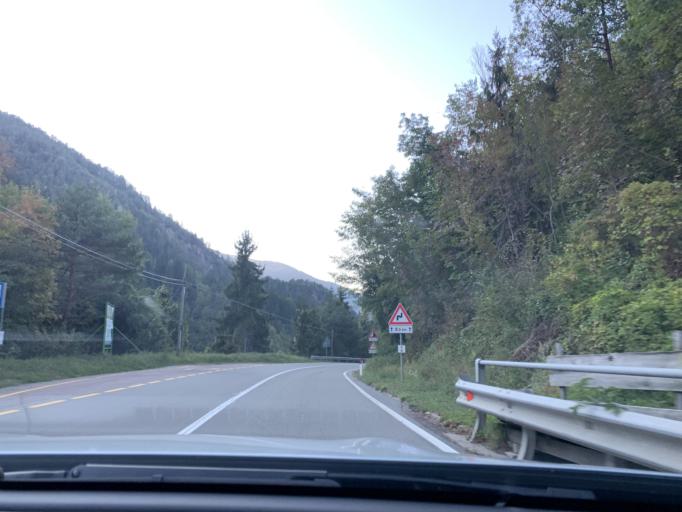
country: IT
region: Trentino-Alto Adige
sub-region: Bolzano
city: Nova Ponente
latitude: 46.4487
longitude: 11.4503
